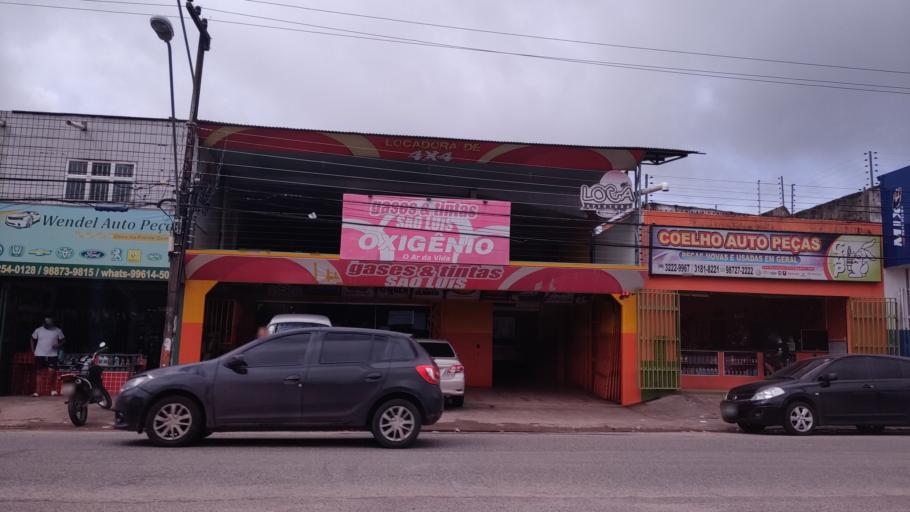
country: BR
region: Maranhao
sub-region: Sao Luis
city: Sao Luis
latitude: -2.5418
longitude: -44.2848
